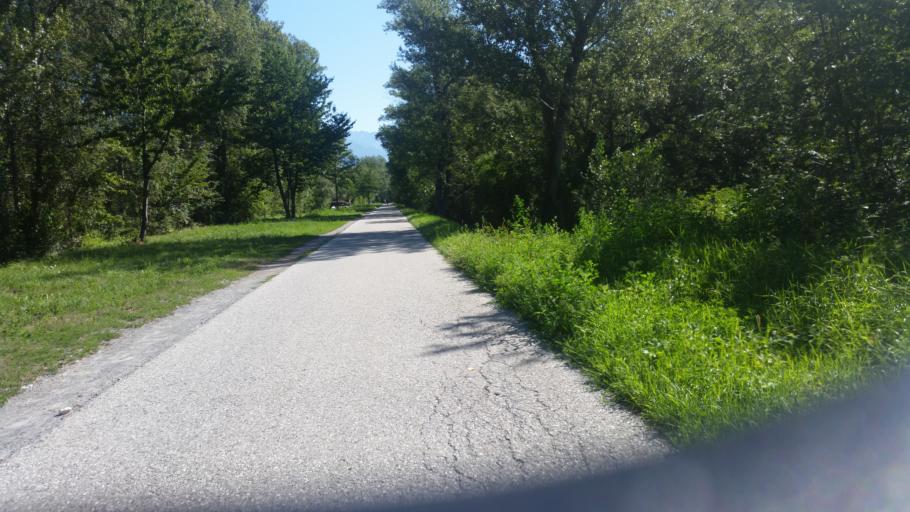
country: CH
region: Valais
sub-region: Sierre District
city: Chermignon-d'en Haut
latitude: 46.2700
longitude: 7.4800
